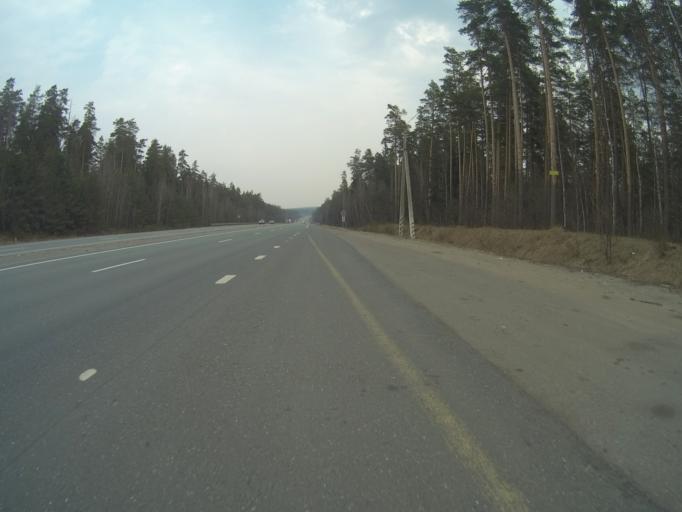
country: RU
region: Vladimir
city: Kommunar
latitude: 56.0652
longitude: 40.4591
